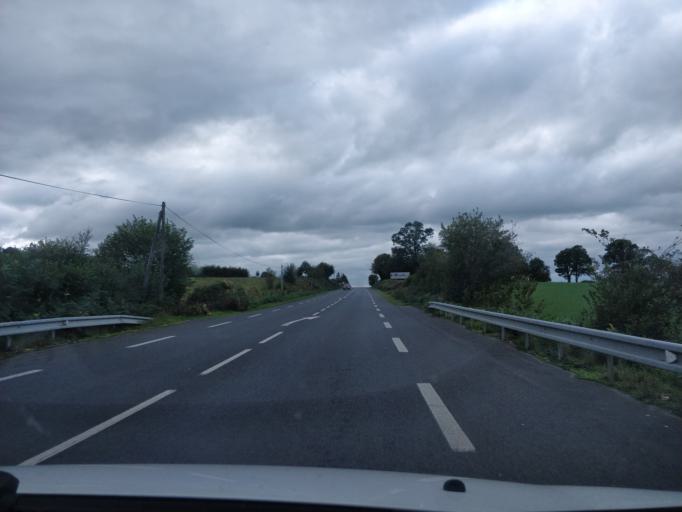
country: FR
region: Lower Normandy
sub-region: Departement de la Manche
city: Villedieu-les-Poeles
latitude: 48.8311
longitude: -1.1694
